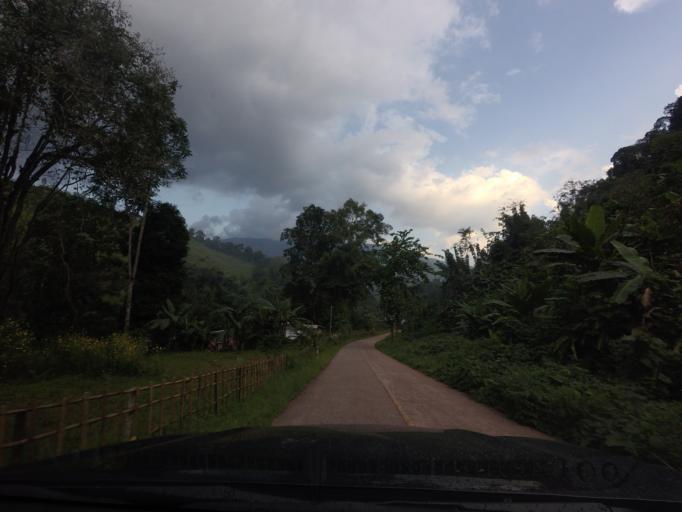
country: TH
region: Nan
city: Bo Kluea
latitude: 19.1940
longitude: 101.1950
